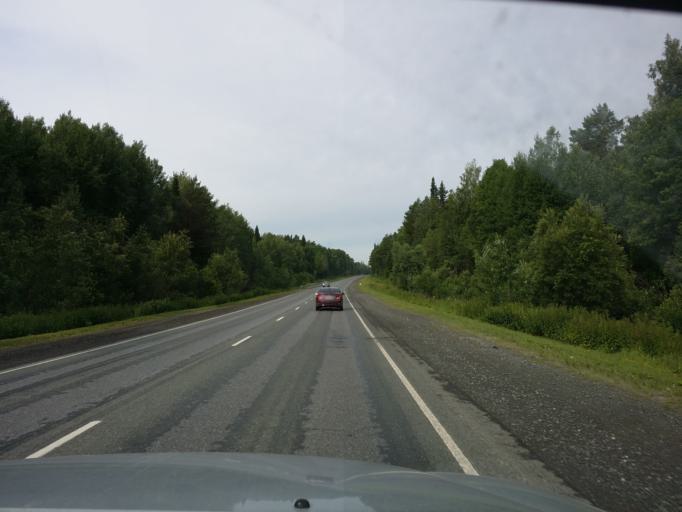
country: RU
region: Tjumen
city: Abalak
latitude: 58.4780
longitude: 68.6155
